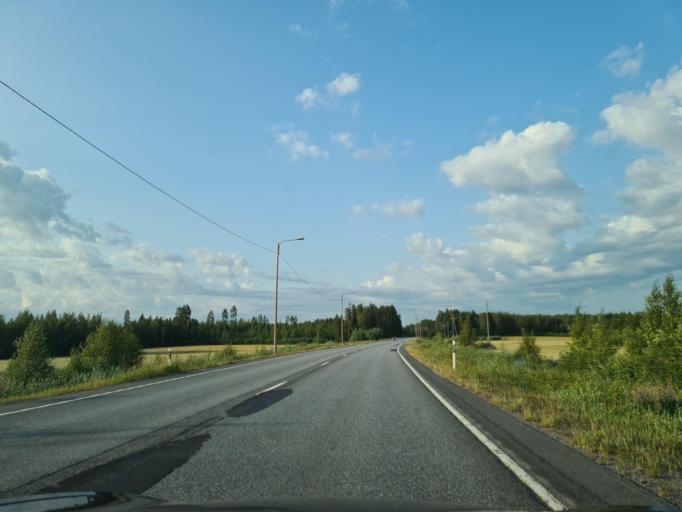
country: FI
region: Southern Ostrobothnia
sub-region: Seinaejoki
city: Kauhava
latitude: 63.0685
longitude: 23.0470
